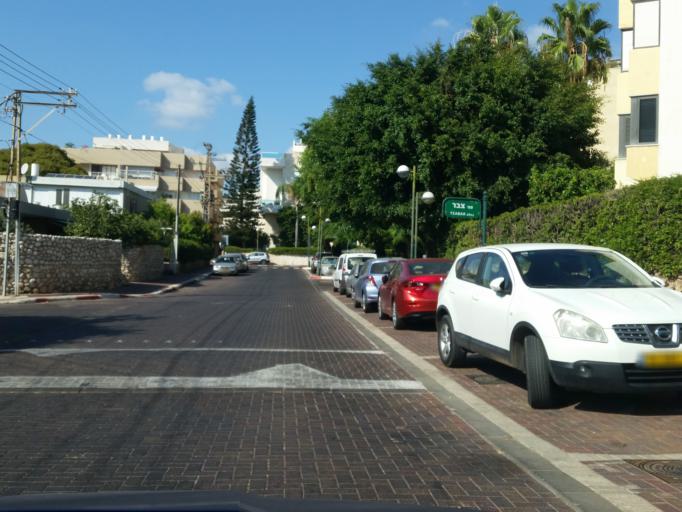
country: IL
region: Tel Aviv
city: Ramat HaSharon
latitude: 32.1396
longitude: 34.8392
